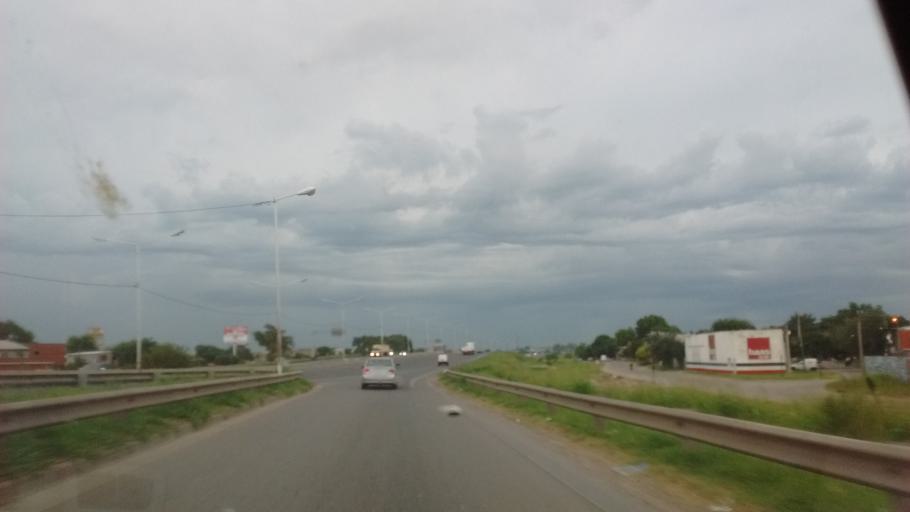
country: AR
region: Santa Fe
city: Perez
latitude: -32.9685
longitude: -60.7177
